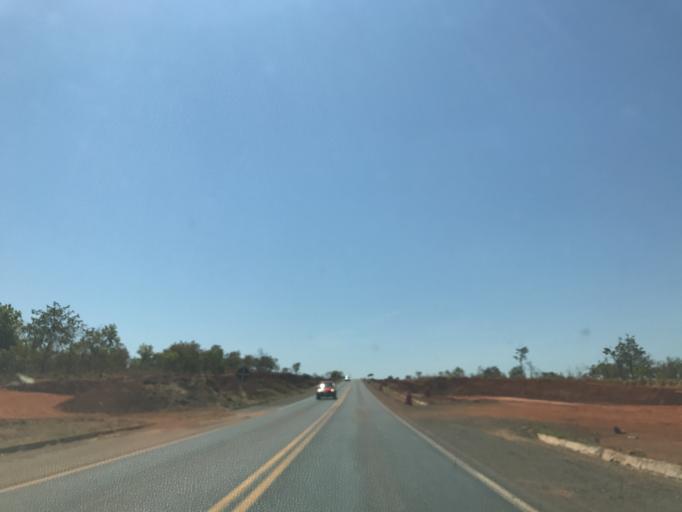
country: BR
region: Minas Gerais
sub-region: Prata
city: Prata
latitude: -19.4361
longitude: -48.8888
